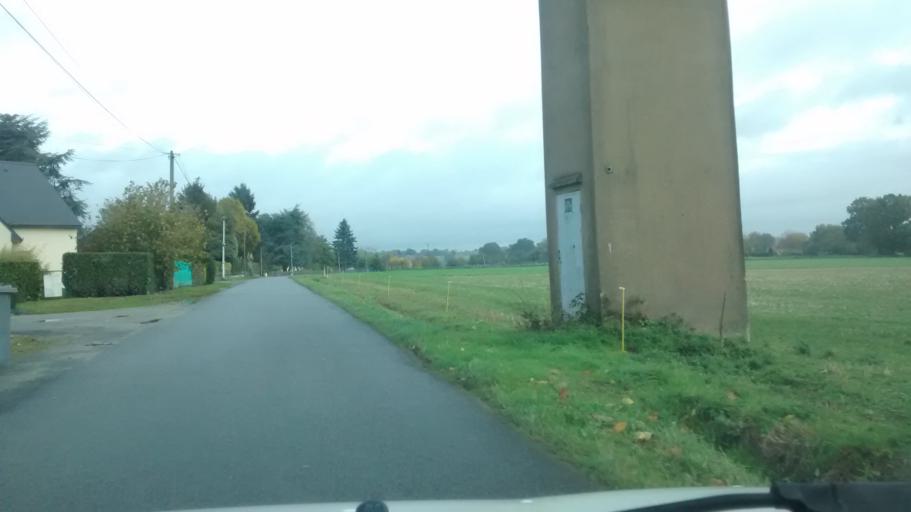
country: FR
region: Brittany
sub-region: Departement d'Ille-et-Vilaine
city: Chateaubourg
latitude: 48.1178
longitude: -1.3953
